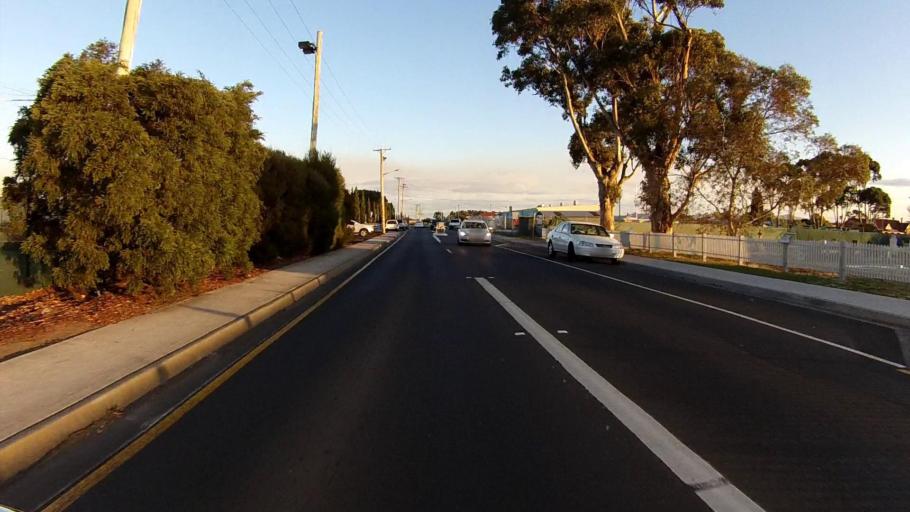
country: AU
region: Tasmania
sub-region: Sorell
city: Sorell
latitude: -42.7836
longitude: 147.5645
